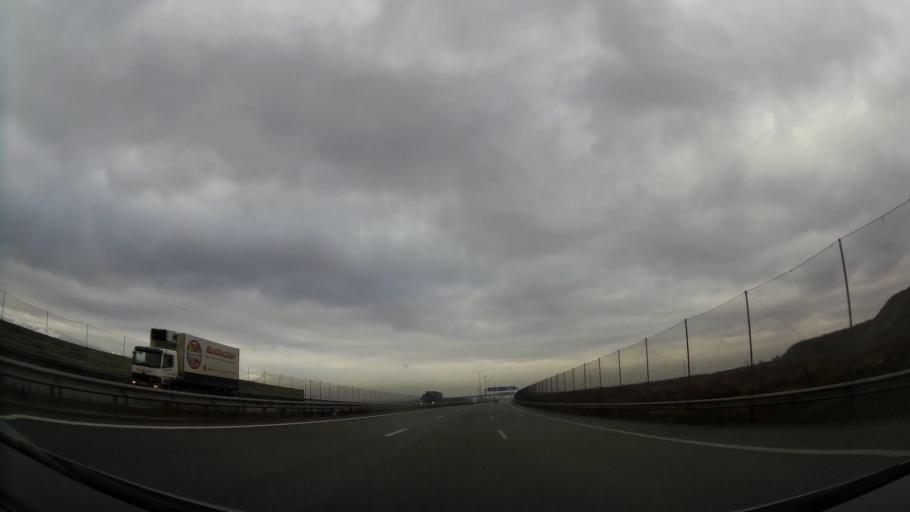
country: BG
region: Sofia-Capital
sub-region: Stolichna Obshtina
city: Sofia
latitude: 42.7196
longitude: 23.4026
